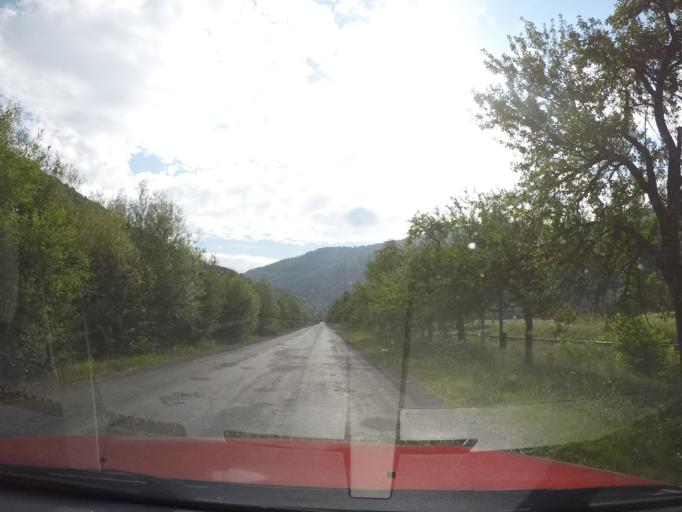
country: UA
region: Zakarpattia
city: Velykyi Bereznyi
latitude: 48.9405
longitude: 22.4774
